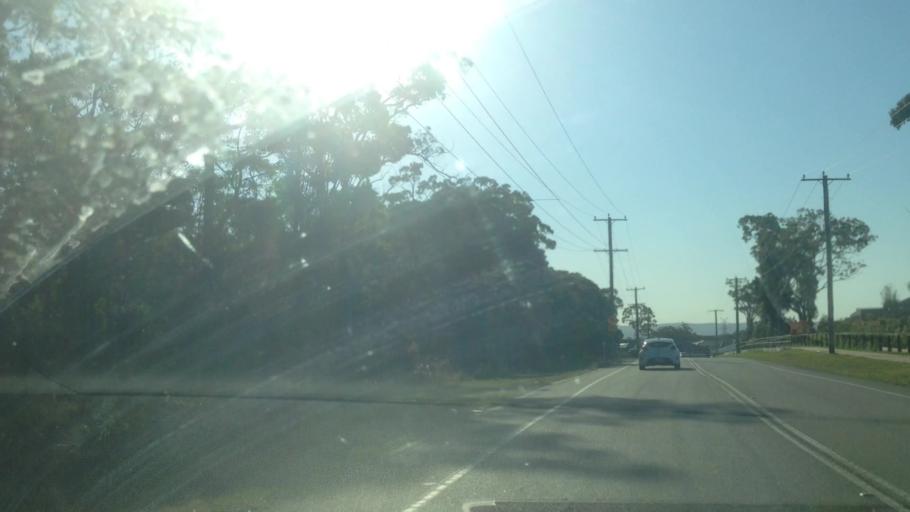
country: AU
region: New South Wales
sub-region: Lake Macquarie Shire
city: Dora Creek
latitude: -33.1119
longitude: 151.5099
